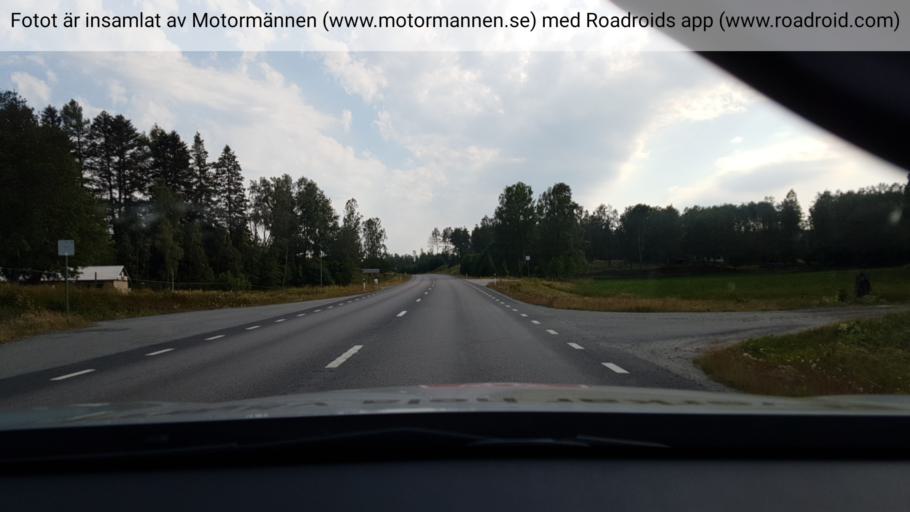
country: SE
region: Vaestra Goetaland
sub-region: Ulricehamns Kommun
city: Ulricehamn
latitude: 57.9539
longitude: 13.5191
